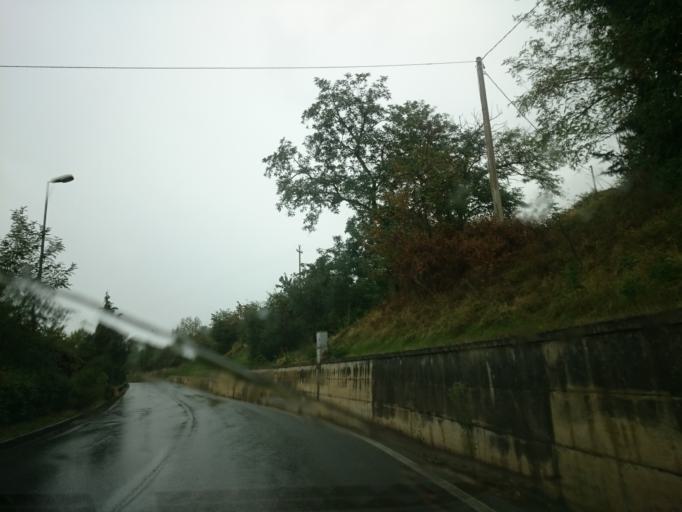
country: IT
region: Tuscany
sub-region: Province of Florence
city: Reggello
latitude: 43.7070
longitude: 11.5225
